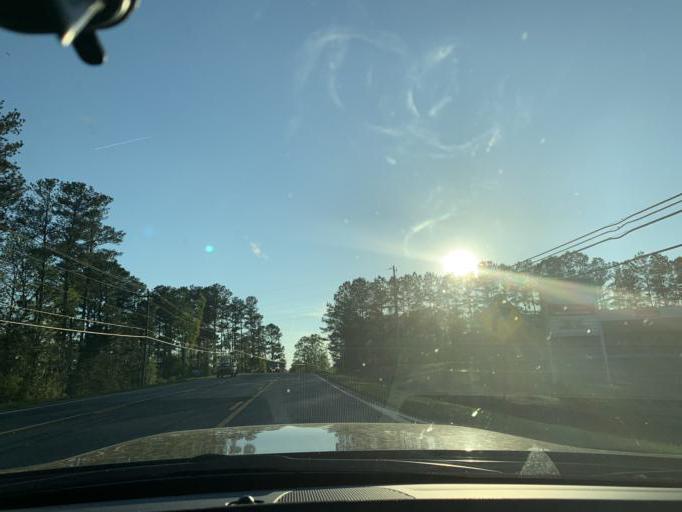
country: US
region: Georgia
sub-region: Forsyth County
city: Cumming
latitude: 34.2376
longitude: -84.2022
